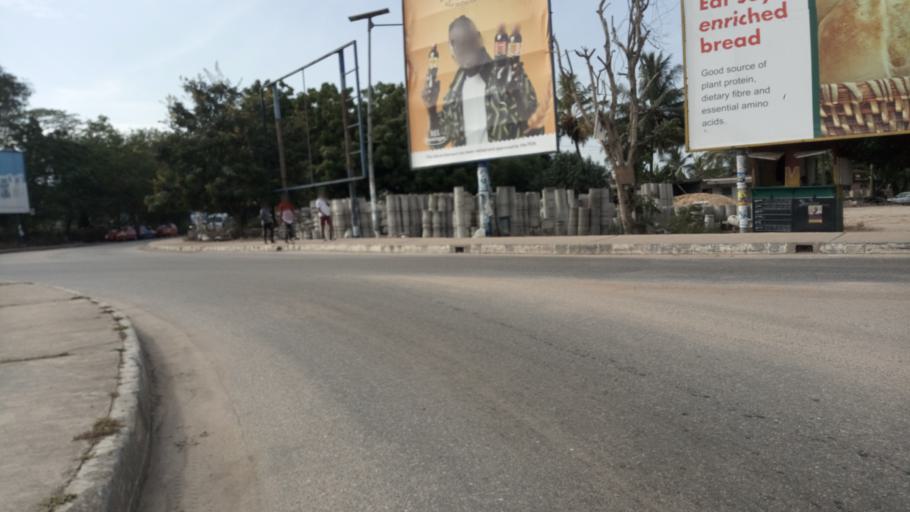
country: GH
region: Central
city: Winneba
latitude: 5.3836
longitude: -0.6425
